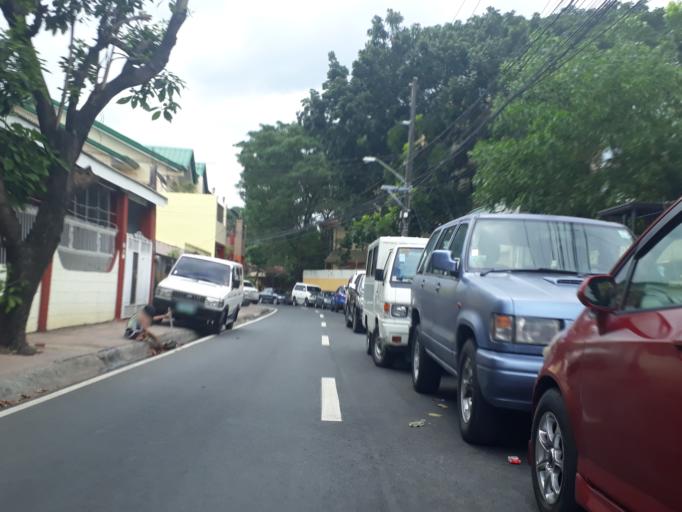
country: PH
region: Calabarzon
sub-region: Province of Rizal
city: Antipolo
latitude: 14.6438
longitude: 121.1177
